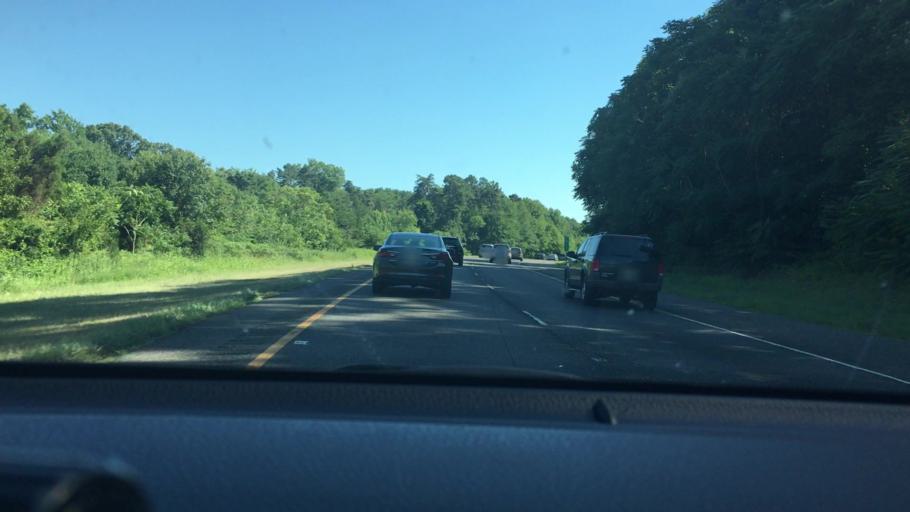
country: US
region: New Jersey
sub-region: Camden County
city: Blackwood
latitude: 39.8058
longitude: -75.1051
